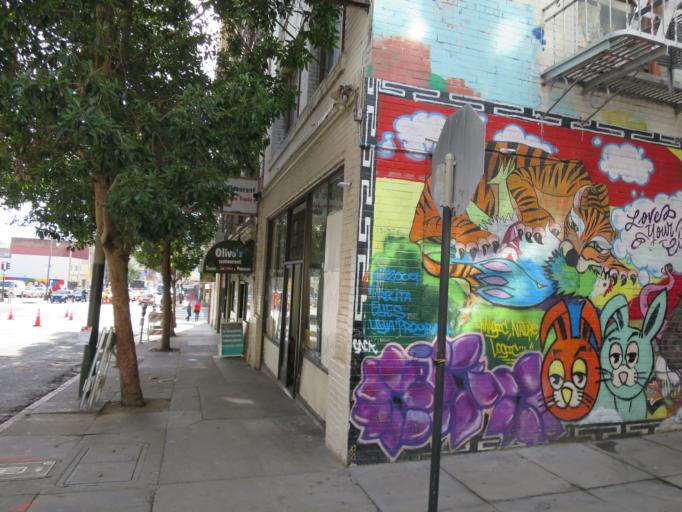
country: US
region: California
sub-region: San Francisco County
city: San Francisco
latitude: 37.7875
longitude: -122.4185
